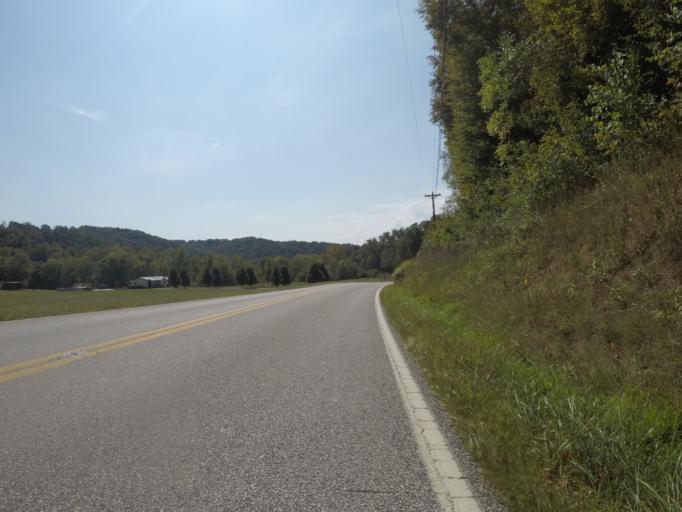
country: US
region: West Virginia
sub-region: Cabell County
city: Lesage
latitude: 38.5257
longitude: -82.3896
